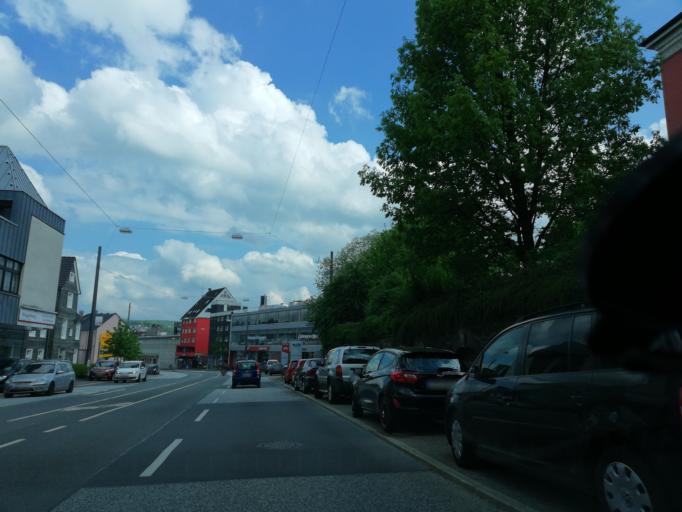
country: DE
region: North Rhine-Westphalia
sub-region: Regierungsbezirk Dusseldorf
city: Wuppertal
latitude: 51.2713
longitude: 7.2147
